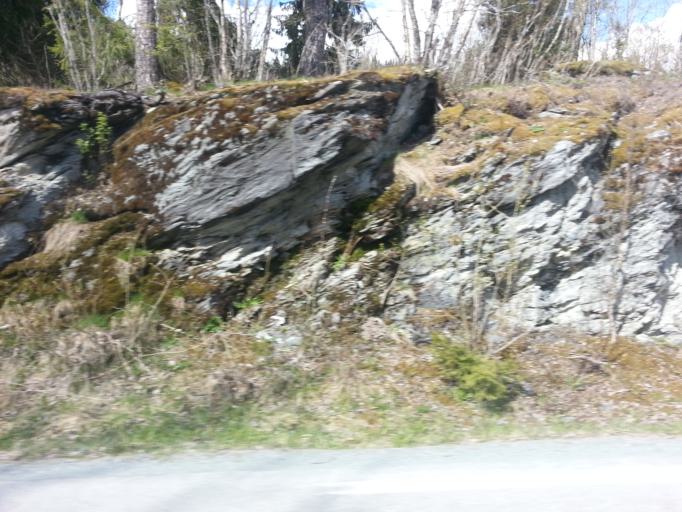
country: NO
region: Nord-Trondelag
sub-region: Levanger
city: Skogn
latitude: 63.6371
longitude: 11.2370
